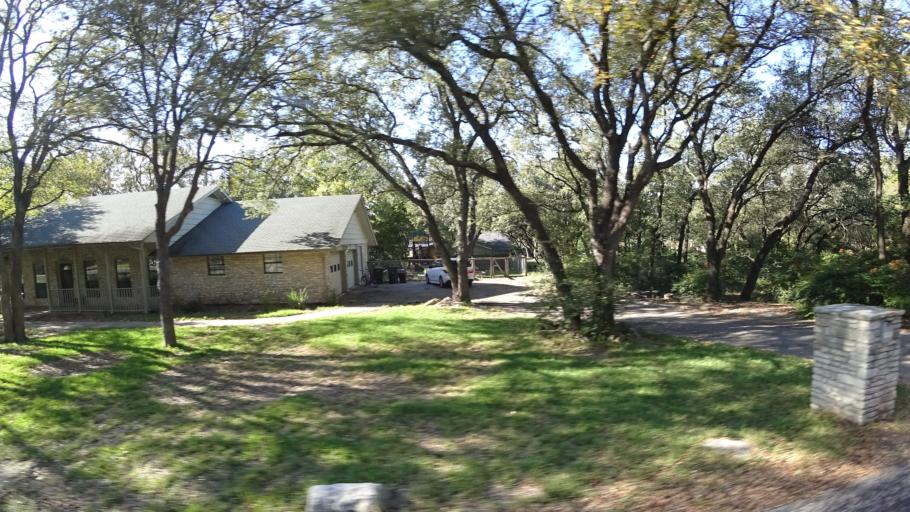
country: US
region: Texas
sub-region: Williamson County
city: Jollyville
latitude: 30.4244
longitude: -97.7805
